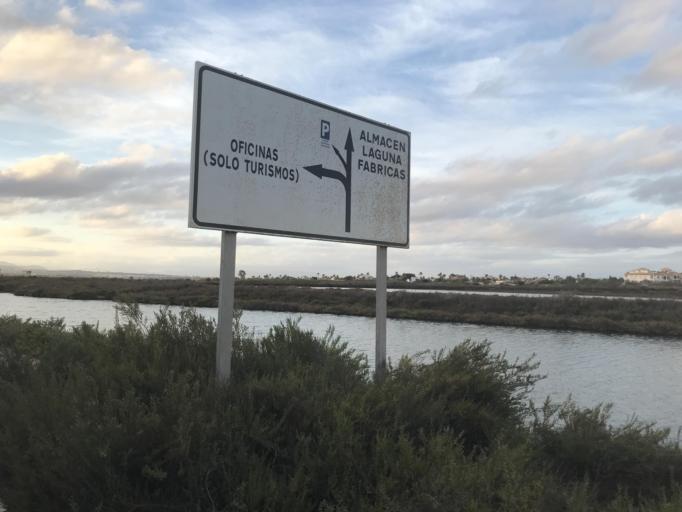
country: ES
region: Valencia
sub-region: Provincia de Alicante
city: Torrevieja
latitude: 37.9787
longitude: -0.6965
